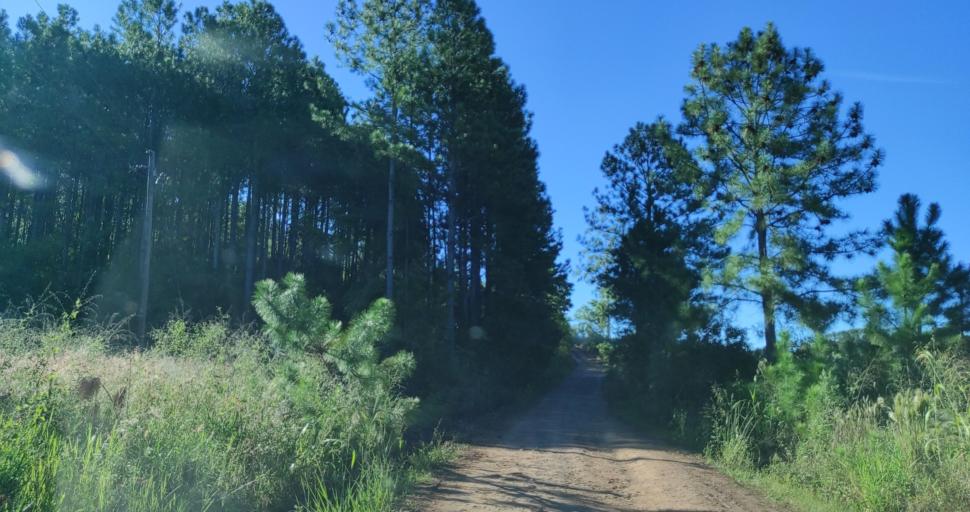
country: AR
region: Misiones
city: Capiovi
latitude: -26.9064
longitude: -54.9967
